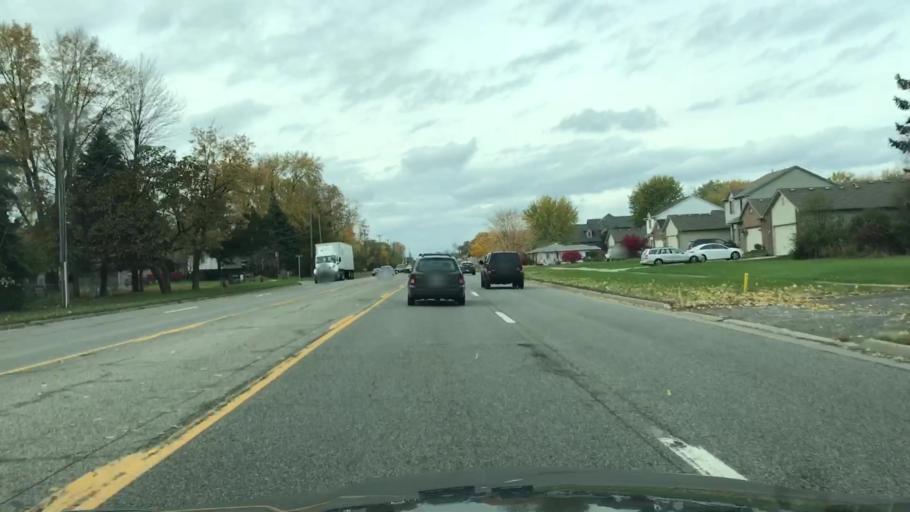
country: US
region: Michigan
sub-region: Oakland County
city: Clawson
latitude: 42.5493
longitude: -83.1011
